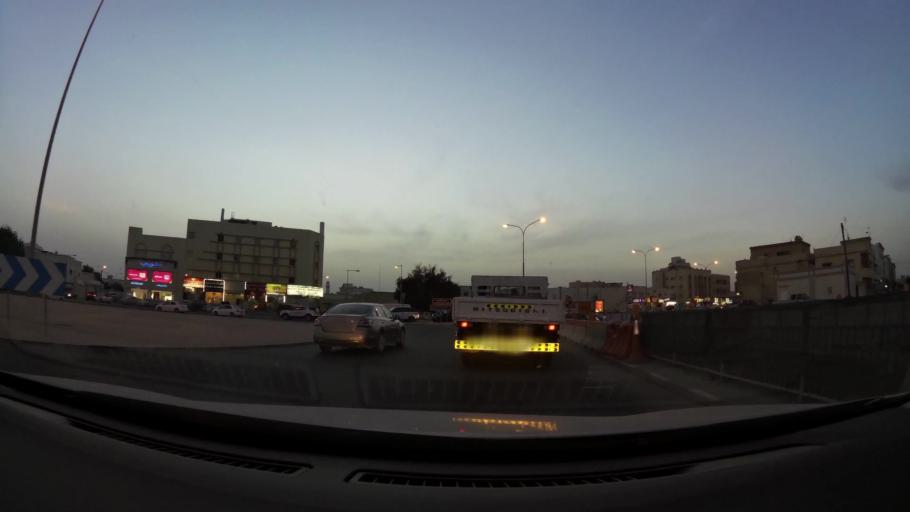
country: QA
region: Al Wakrah
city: Al Wakrah
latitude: 25.1611
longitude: 51.5987
